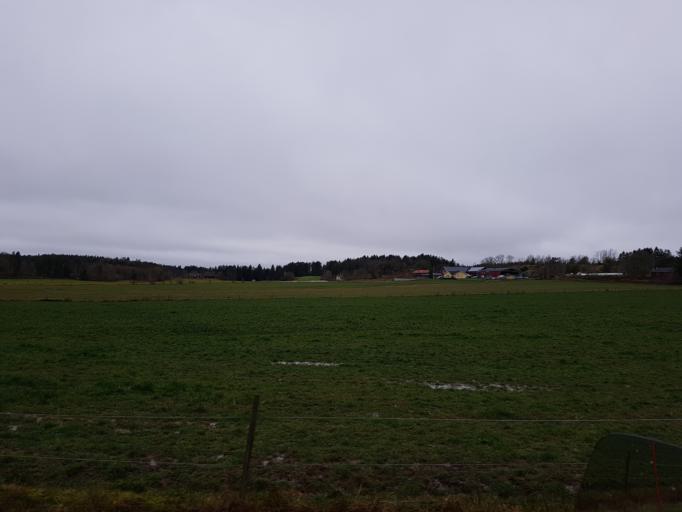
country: SE
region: Vaestra Goetaland
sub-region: Orust
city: Henan
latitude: 58.2134
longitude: 11.7718
